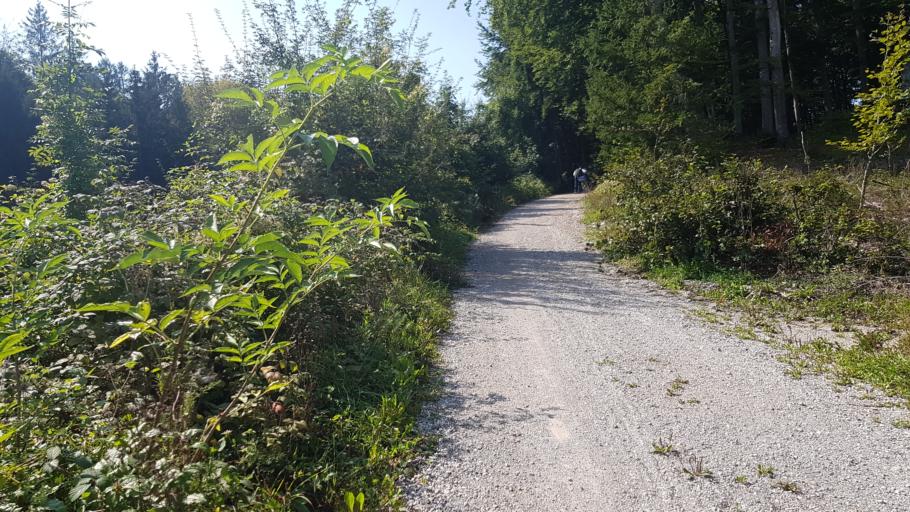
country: DE
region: Bavaria
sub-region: Upper Bavaria
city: Worthsee
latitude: 48.0649
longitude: 11.2171
